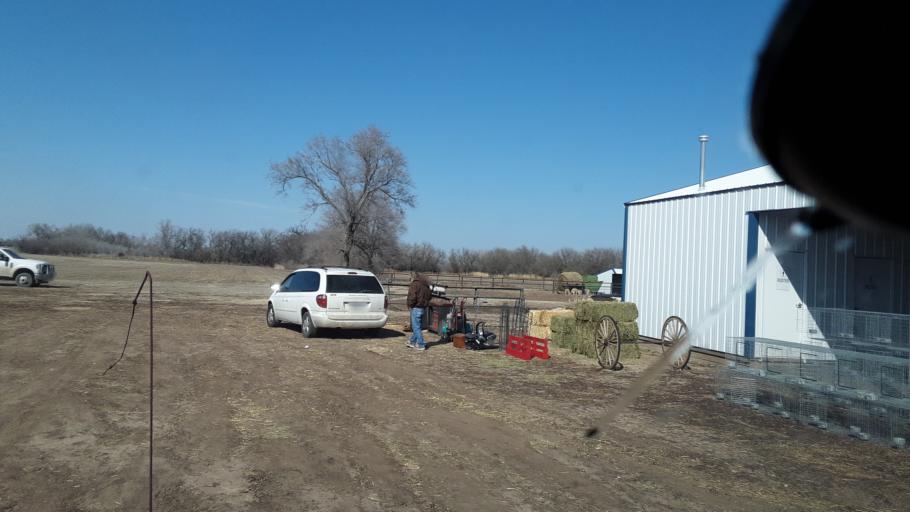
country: US
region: Kansas
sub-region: Reno County
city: South Hutchinson
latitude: 37.9413
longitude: -97.8937
